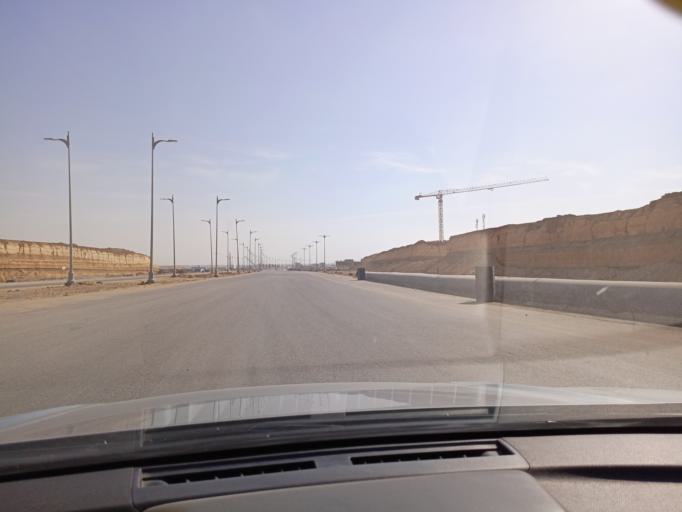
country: EG
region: Muhafazat al Qalyubiyah
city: Al Khankah
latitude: 30.0314
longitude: 31.6802
